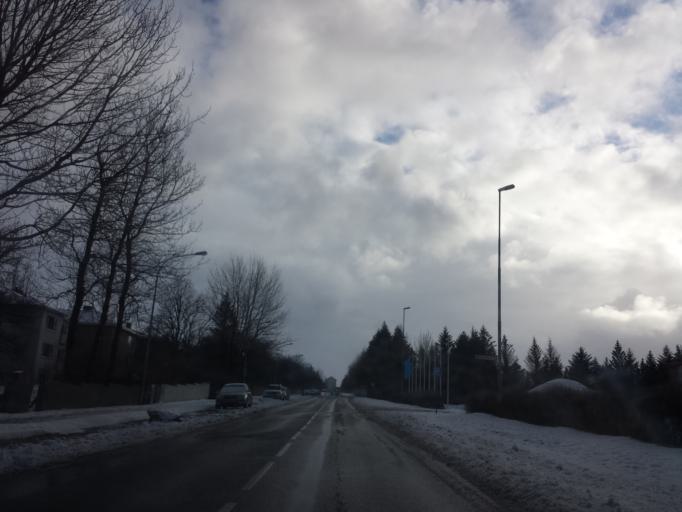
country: IS
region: Capital Region
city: Reykjavik
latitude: 64.1387
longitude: -21.9146
